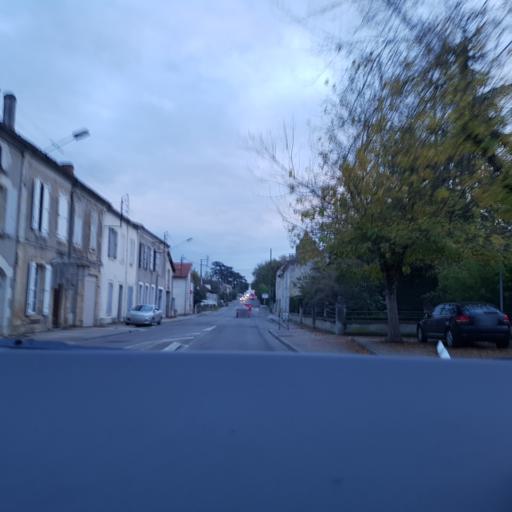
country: FR
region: Midi-Pyrenees
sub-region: Departement du Gers
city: Condom
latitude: 43.9547
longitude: 0.3643
